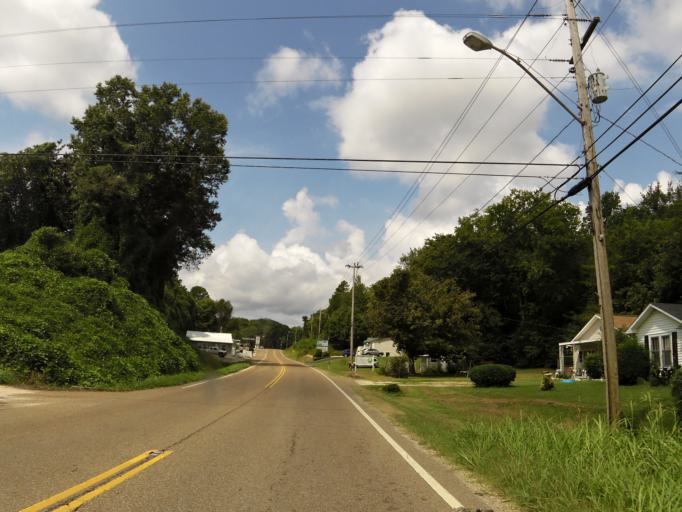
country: US
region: Tennessee
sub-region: Perry County
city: Linden
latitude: 35.6175
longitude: -87.8433
